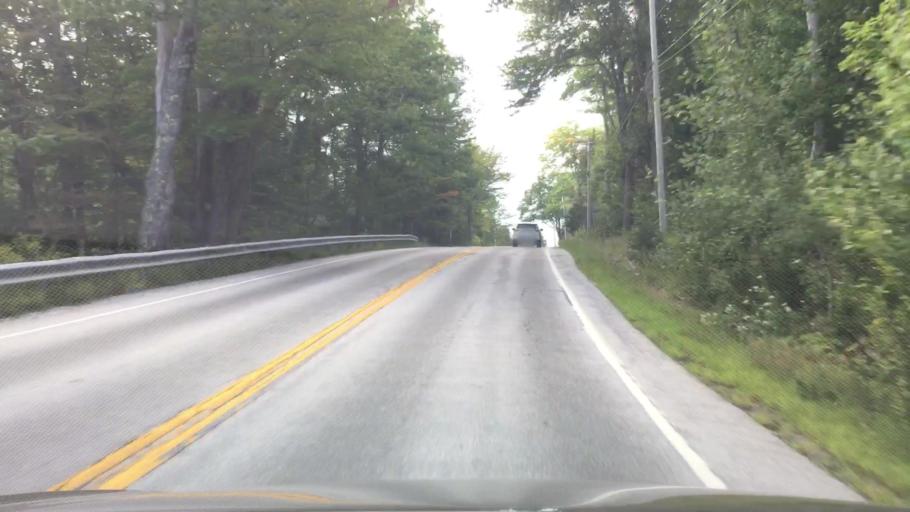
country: US
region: Maine
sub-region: Hancock County
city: Penobscot
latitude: 44.4263
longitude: -68.6010
